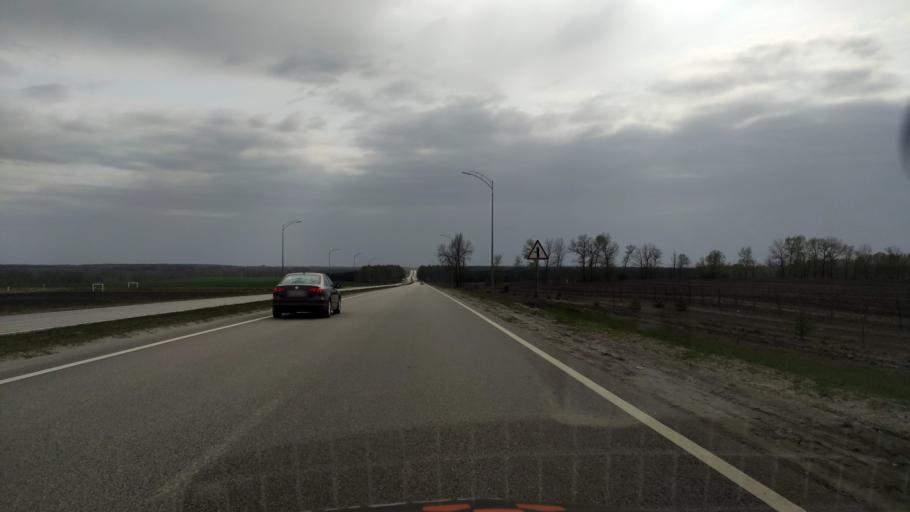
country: RU
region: Belgorod
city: Staryy Oskol
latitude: 51.4182
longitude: 37.8896
